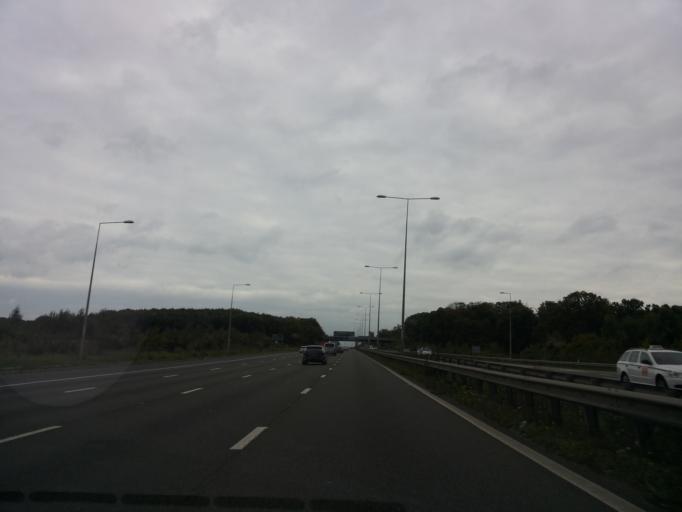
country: GB
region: England
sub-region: Kent
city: Gravesend
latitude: 51.4045
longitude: 0.3984
